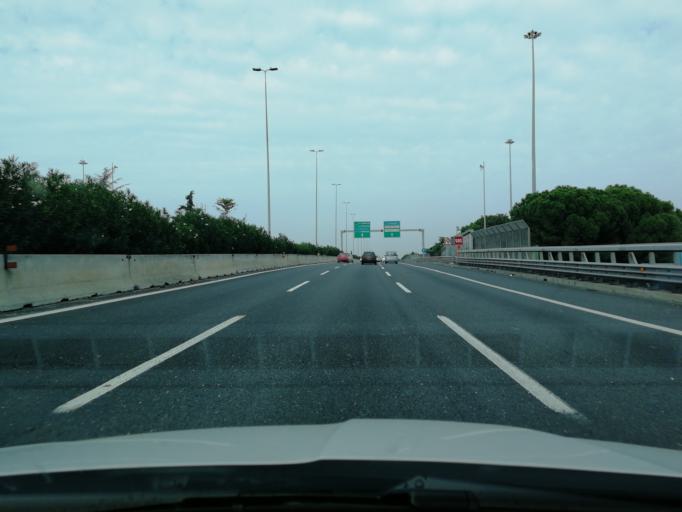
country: IT
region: Latium
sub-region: Citta metropolitana di Roma Capitale
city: Ciampino
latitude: 41.8636
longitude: 12.6007
